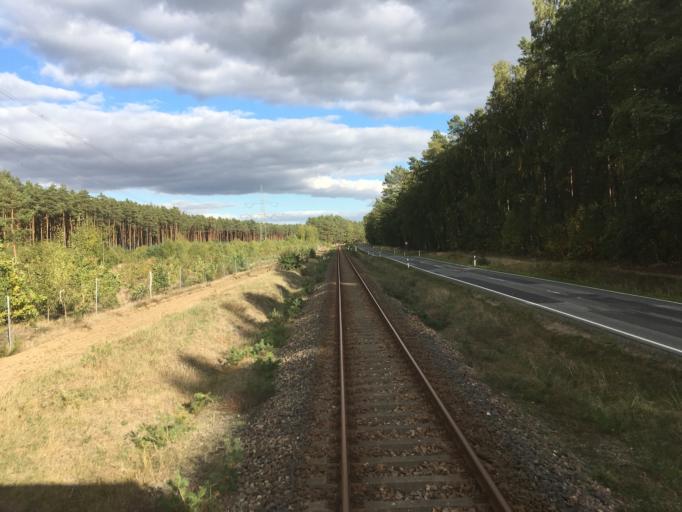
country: DE
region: Mecklenburg-Vorpommern
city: Malchow
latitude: 53.5320
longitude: 12.4937
